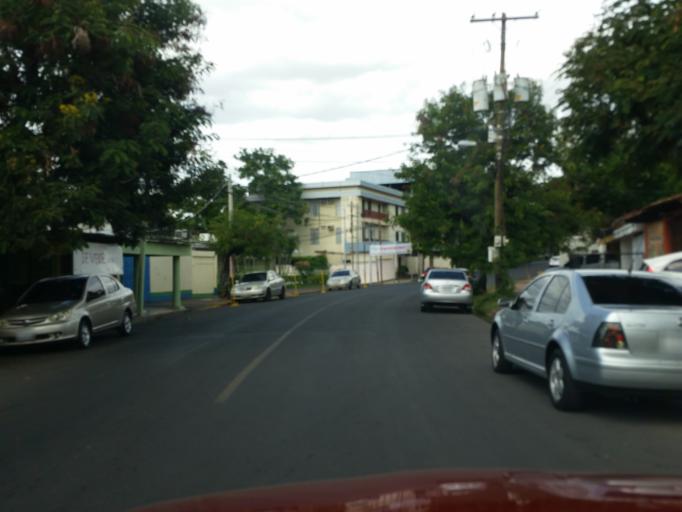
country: NI
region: Managua
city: Managua
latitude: 12.1422
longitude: -86.2777
